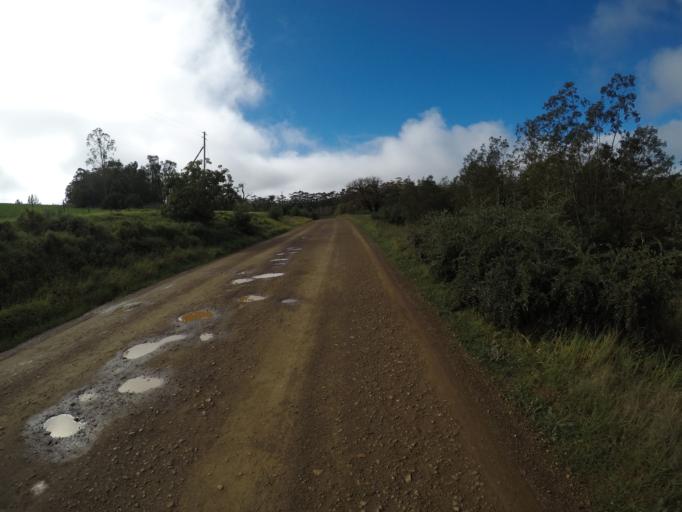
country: ZA
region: Western Cape
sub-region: Cape Winelands District Municipality
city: Ashton
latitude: -34.1124
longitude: 19.7944
